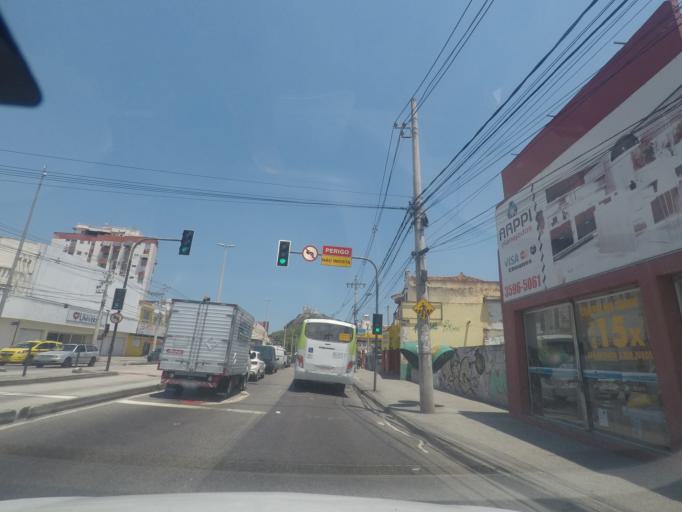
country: BR
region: Rio de Janeiro
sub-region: Duque De Caxias
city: Duque de Caxias
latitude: -22.8400
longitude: -43.2821
